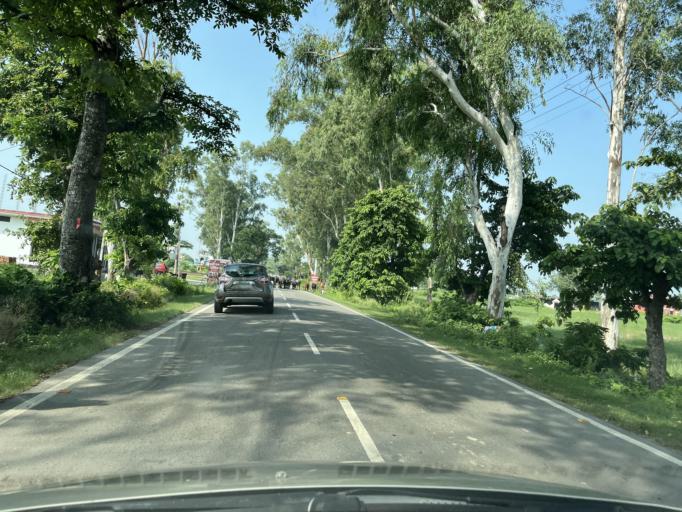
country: IN
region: Uttarakhand
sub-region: Udham Singh Nagar
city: Bazpur
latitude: 29.2123
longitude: 79.2194
